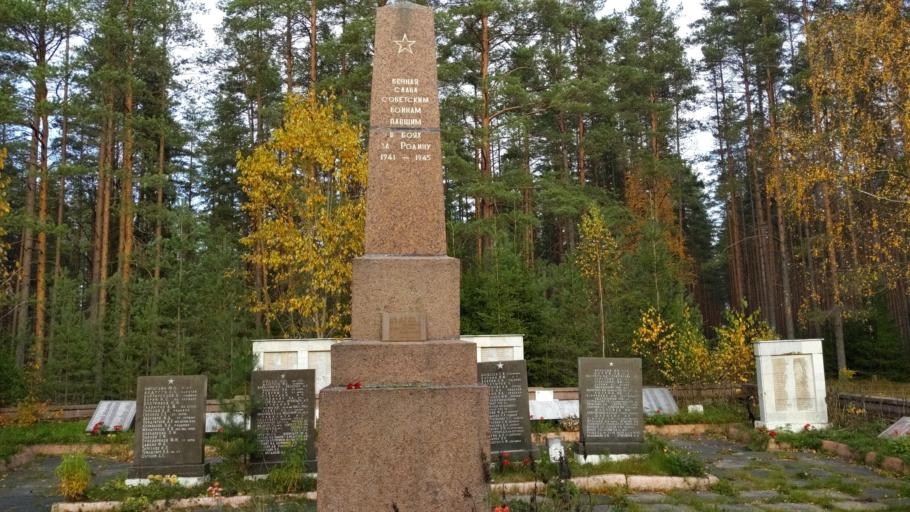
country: RU
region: Leningrad
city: Priladozhskiy
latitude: 59.6368
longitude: 31.4066
